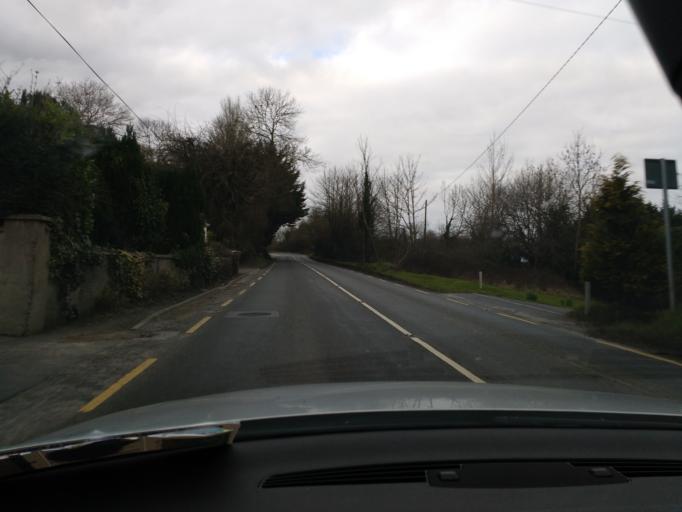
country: IE
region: Leinster
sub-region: Kilkenny
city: Kilkenny
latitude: 52.6889
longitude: -7.2759
